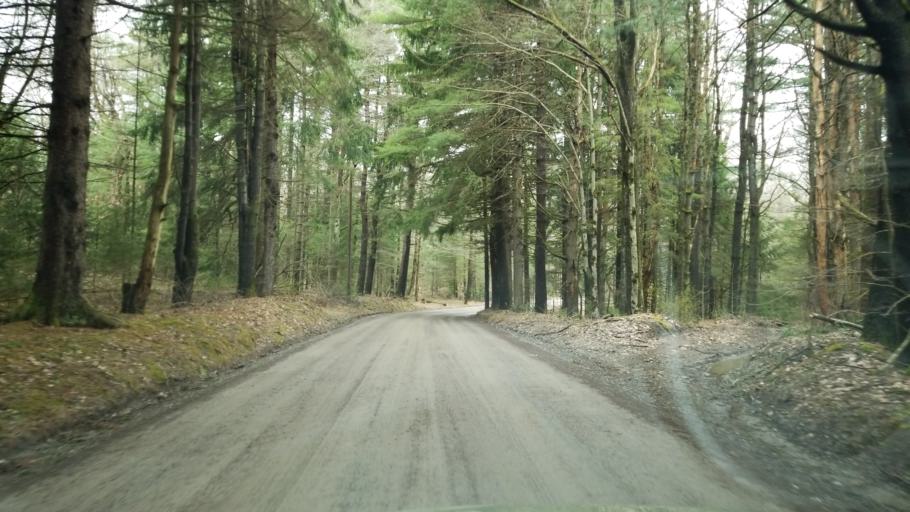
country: US
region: Pennsylvania
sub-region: Clearfield County
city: Shiloh
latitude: 41.1657
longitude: -78.3389
